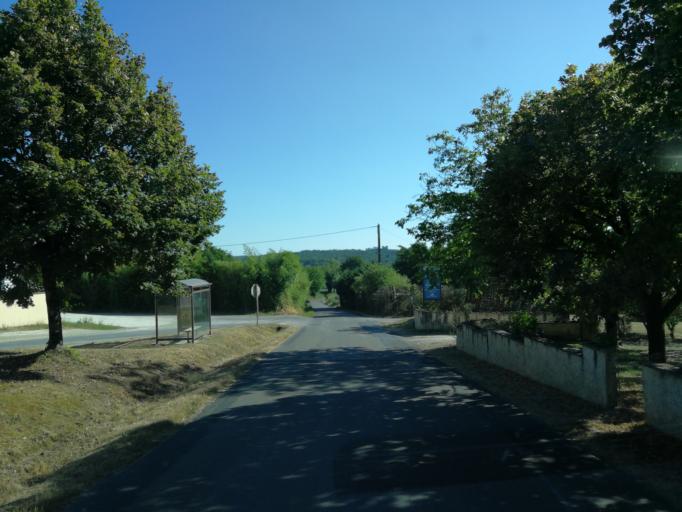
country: FR
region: Midi-Pyrenees
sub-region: Departement du Lot
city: Gourdon
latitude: 44.8042
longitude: 1.3728
